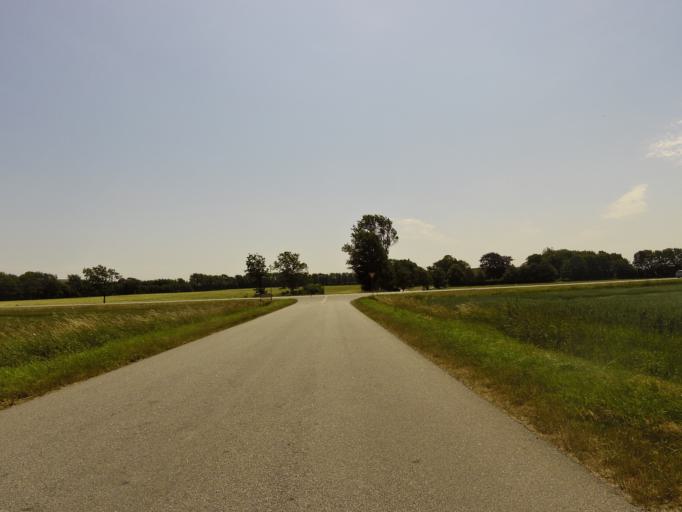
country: DK
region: South Denmark
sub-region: Haderslev Kommune
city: Vojens
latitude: 55.1552
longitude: 9.2516
